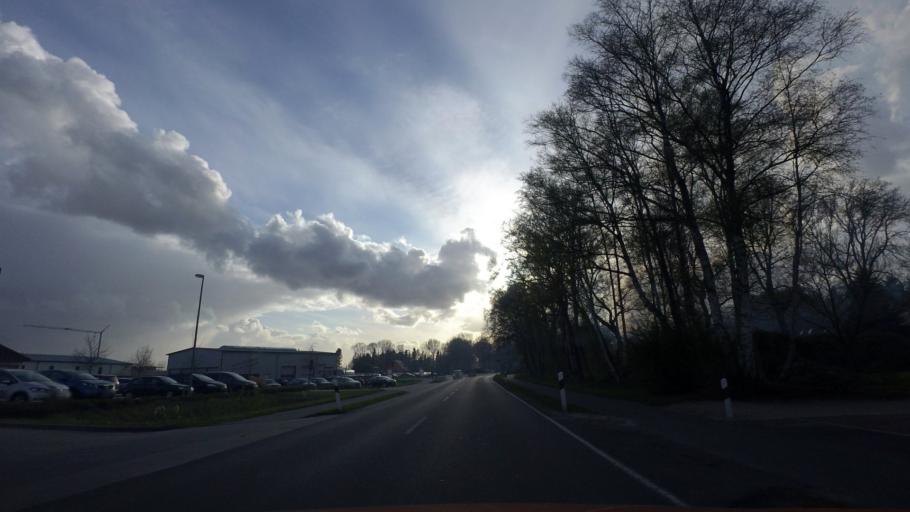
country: DE
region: Lower Saxony
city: Edewecht
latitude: 53.1244
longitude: 8.0849
